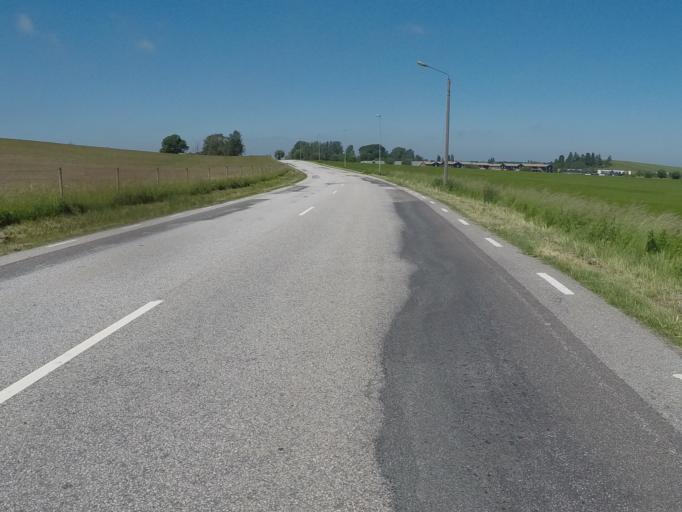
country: SE
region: Skane
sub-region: Malmo
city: Oxie
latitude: 55.5440
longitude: 13.1168
